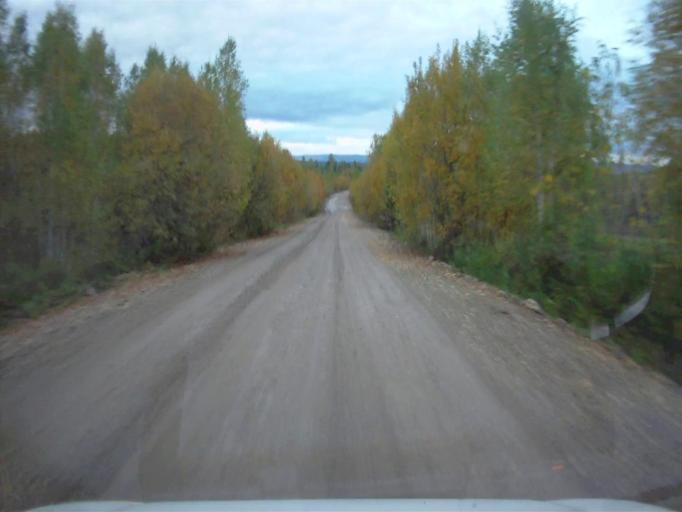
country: RU
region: Sverdlovsk
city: Mikhaylovsk
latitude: 56.2045
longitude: 59.2030
